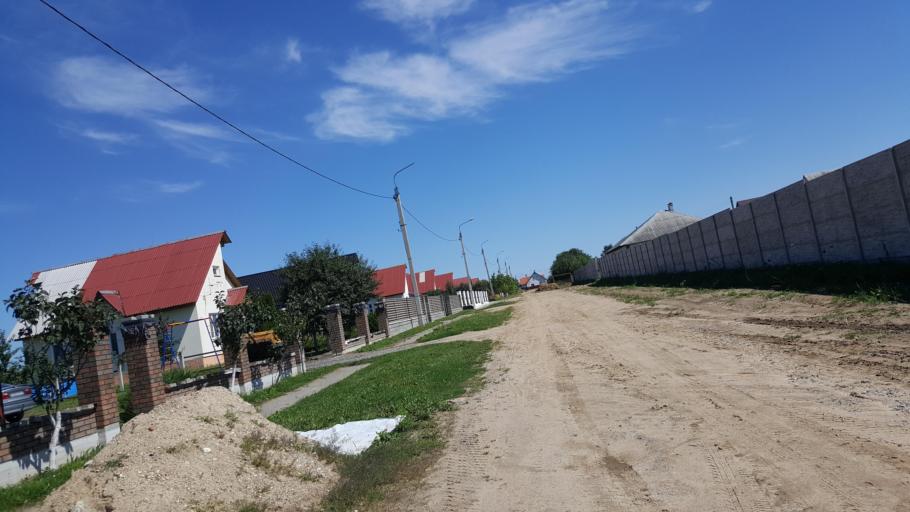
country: BY
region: Brest
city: Charnawchytsy
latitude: 52.2261
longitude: 23.7294
